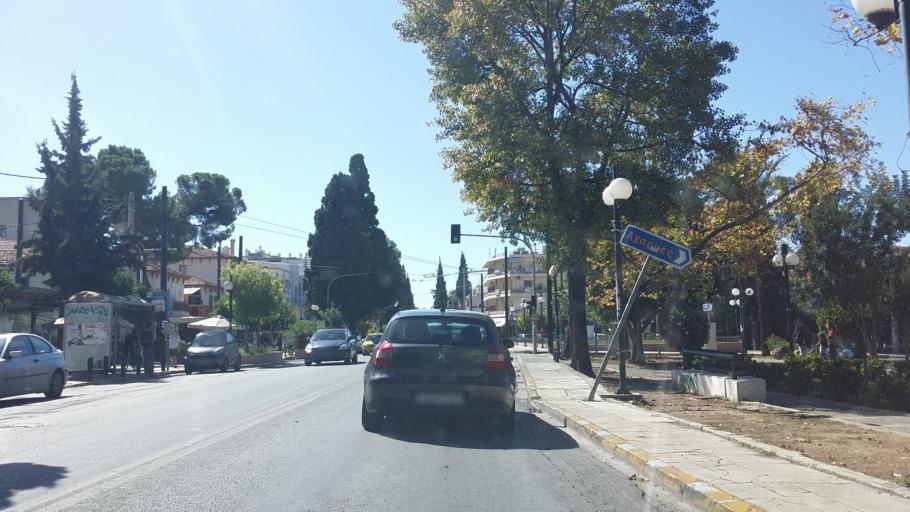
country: GR
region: Attica
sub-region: Nomarchia Athinas
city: Nea Filadelfeia
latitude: 38.0376
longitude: 23.7394
